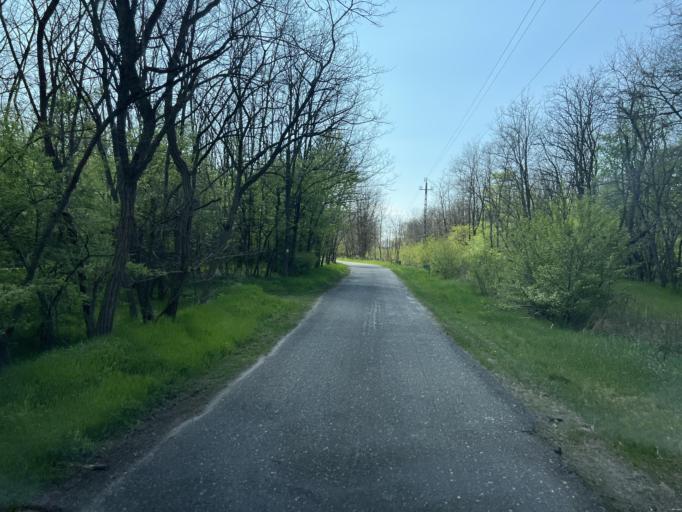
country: HU
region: Pest
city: Inarcs
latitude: 47.2657
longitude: 19.3494
